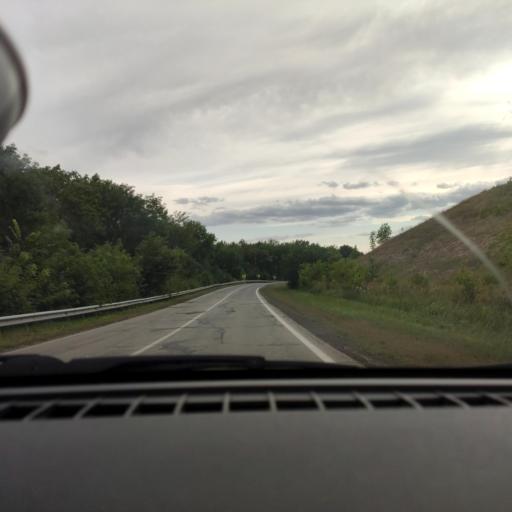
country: RU
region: Samara
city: Krasnyy Yar
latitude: 53.4387
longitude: 50.5874
